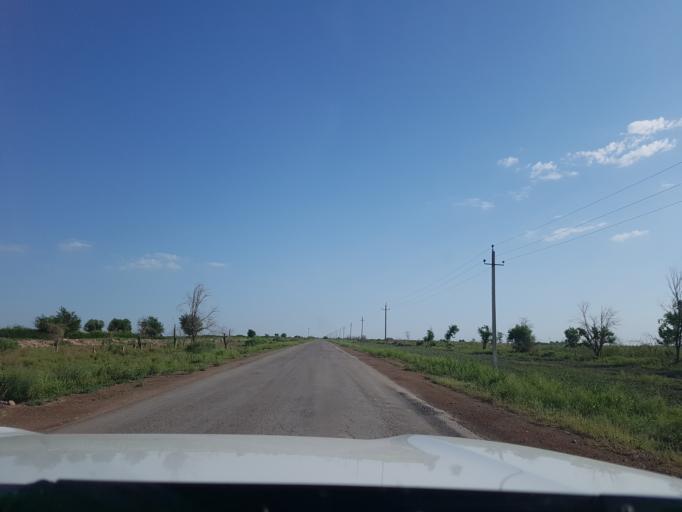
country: TM
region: Dasoguz
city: Koeneuergench
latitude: 41.8684
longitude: 58.7058
